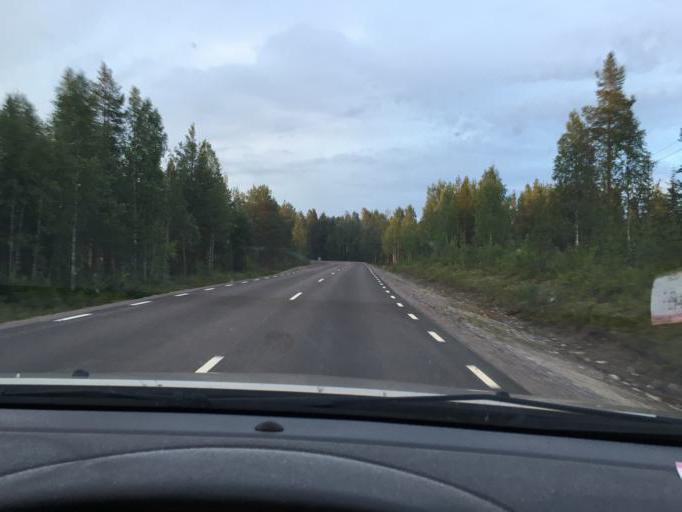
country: SE
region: Norrbotten
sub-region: Lulea Kommun
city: Ranea
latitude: 66.0467
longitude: 22.1975
